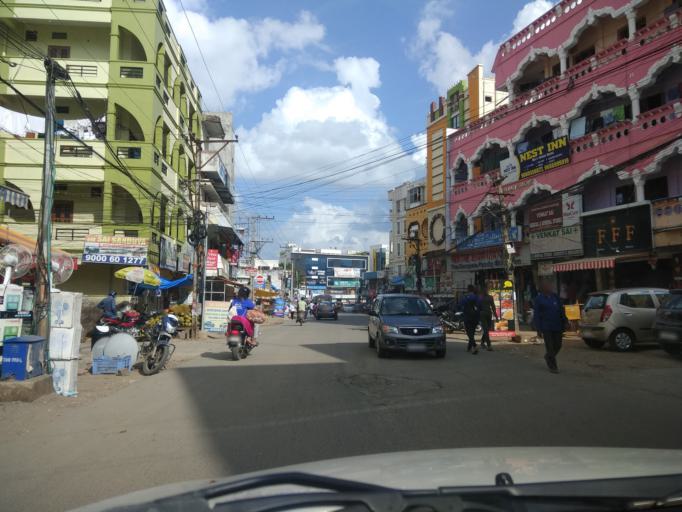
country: IN
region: Telangana
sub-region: Rangareddi
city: Kukatpalli
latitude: 17.4645
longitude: 78.3661
